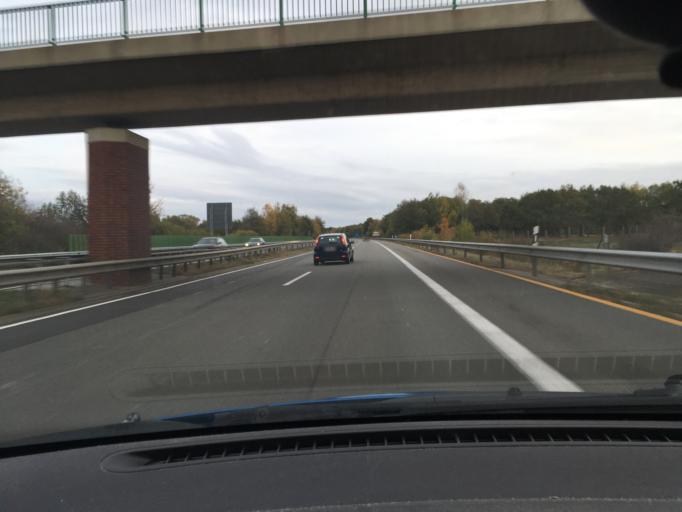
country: DE
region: Lower Saxony
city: Vogelsen
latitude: 53.3052
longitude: 10.3352
